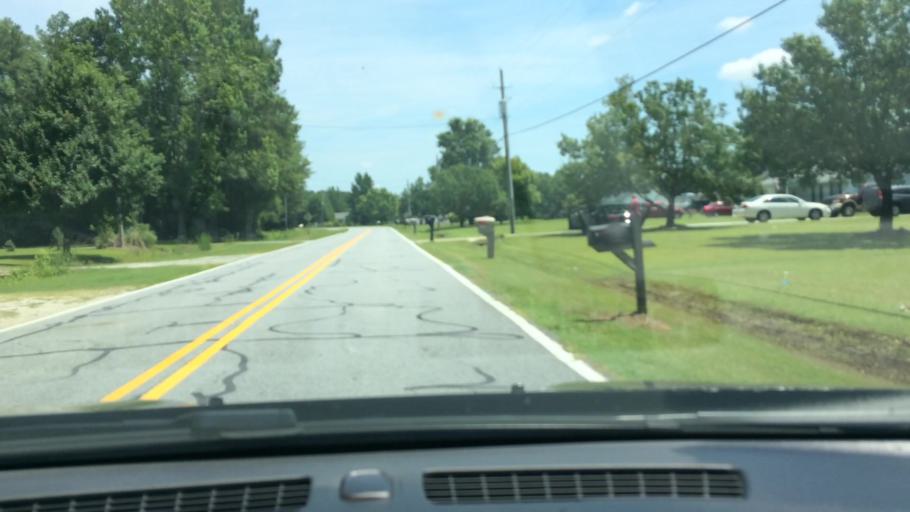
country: US
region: North Carolina
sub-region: Pitt County
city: Windsor
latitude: 35.5043
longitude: -77.3261
